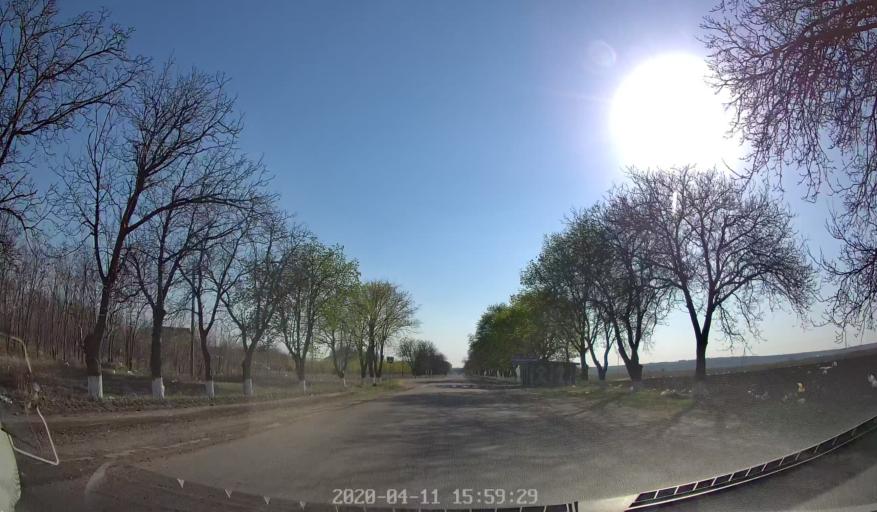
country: MD
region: Chisinau
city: Vadul lui Voda
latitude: 47.0818
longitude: 29.1411
